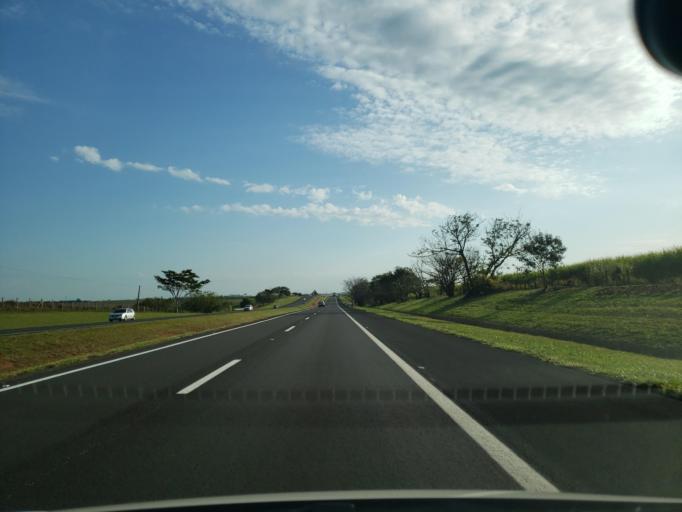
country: BR
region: Sao Paulo
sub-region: Valparaiso
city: Valparaiso
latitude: -21.2061
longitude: -50.8135
